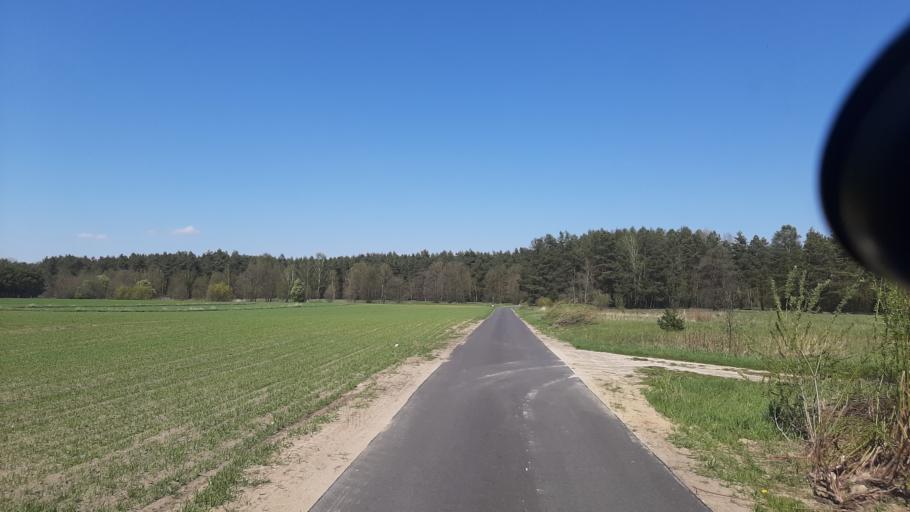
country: PL
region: Lublin Voivodeship
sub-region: Powiat lubelski
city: Garbow
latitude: 51.4058
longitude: 22.3227
